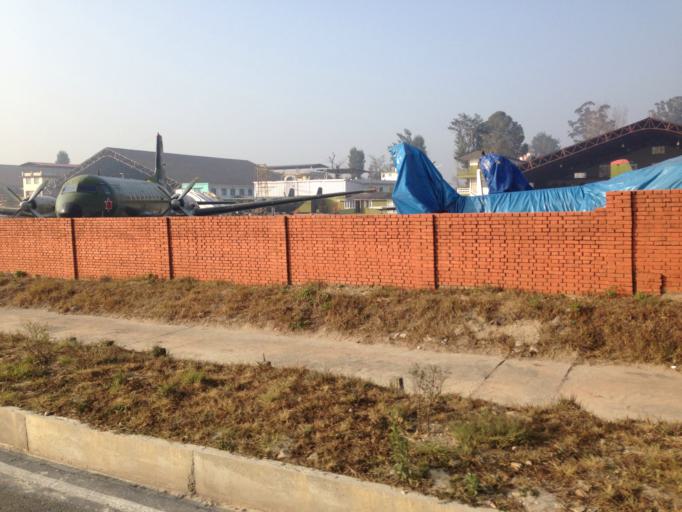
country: NP
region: Central Region
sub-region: Bagmati Zone
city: Kathmandu
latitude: 27.7048
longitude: 85.3597
